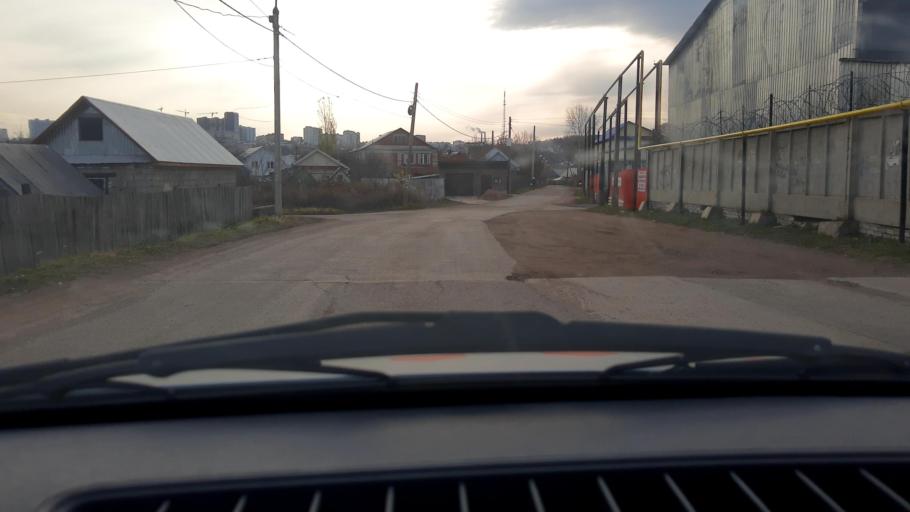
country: RU
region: Bashkortostan
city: Ufa
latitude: 54.7395
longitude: 55.9045
